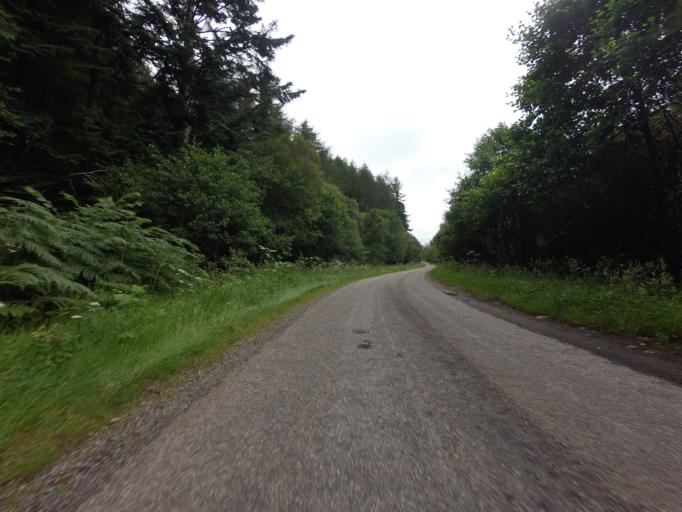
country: GB
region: Scotland
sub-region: Highland
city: Evanton
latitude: 57.9646
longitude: -4.4108
